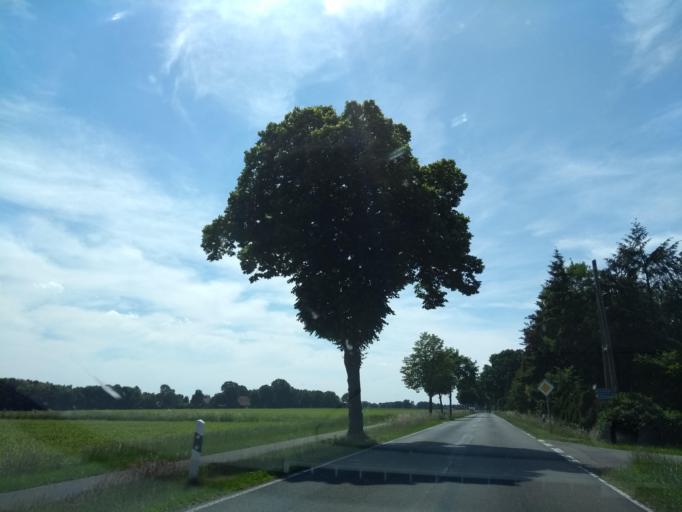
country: DE
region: Lower Saxony
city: Varrel
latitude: 52.6295
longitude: 8.7546
